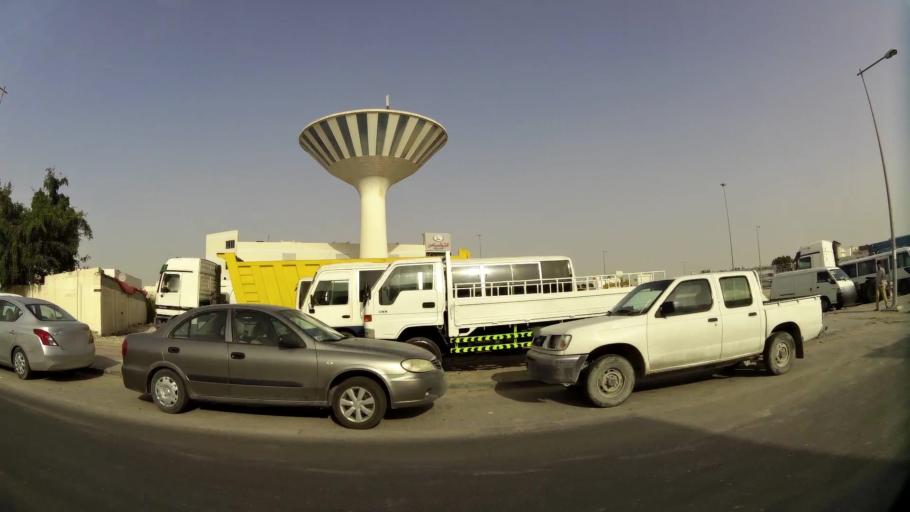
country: QA
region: Baladiyat ar Rayyan
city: Ar Rayyan
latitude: 25.2305
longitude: 51.4383
